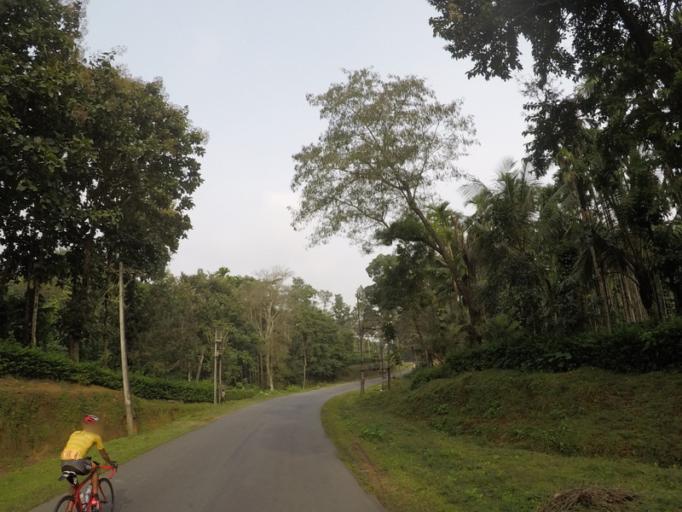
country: IN
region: Karnataka
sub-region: Chikmagalur
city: Chikmagalur
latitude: 13.3335
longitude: 75.5546
